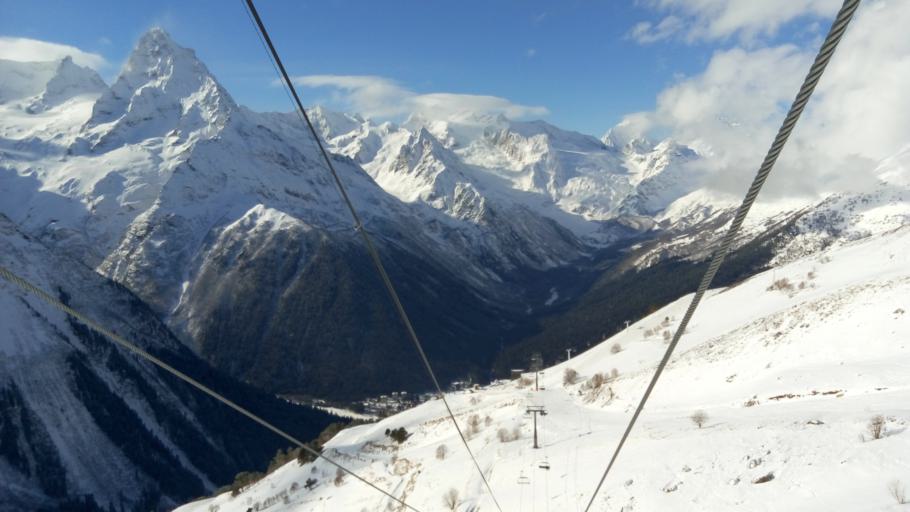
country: RU
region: Karachayevo-Cherkesiya
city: Teberda
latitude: 43.2912
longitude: 41.6567
